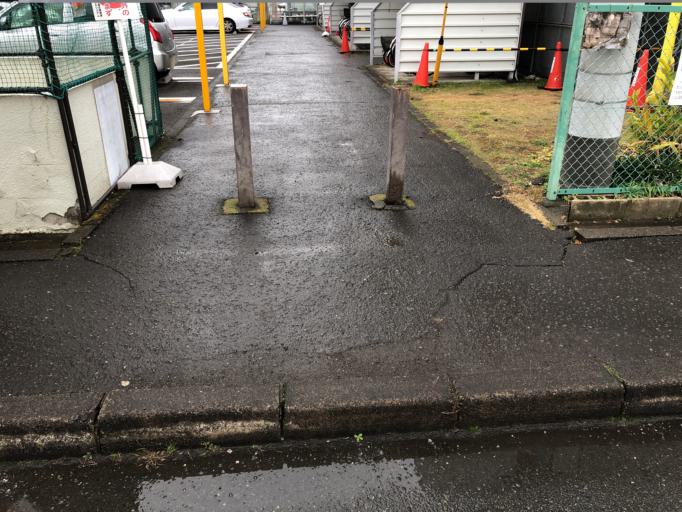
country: JP
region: Kanagawa
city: Minami-rinkan
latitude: 35.5048
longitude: 139.4435
